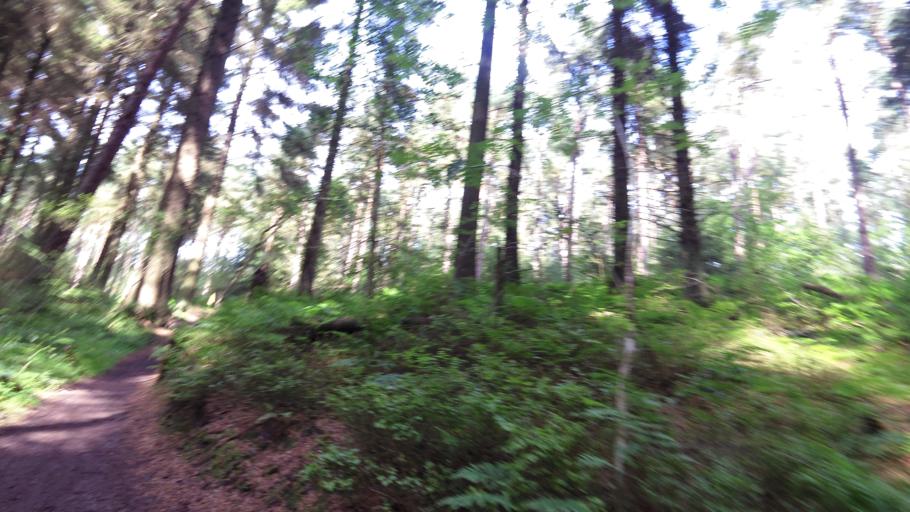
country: GB
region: England
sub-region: North Yorkshire
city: Thornton Dale
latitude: 54.2970
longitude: -0.6324
